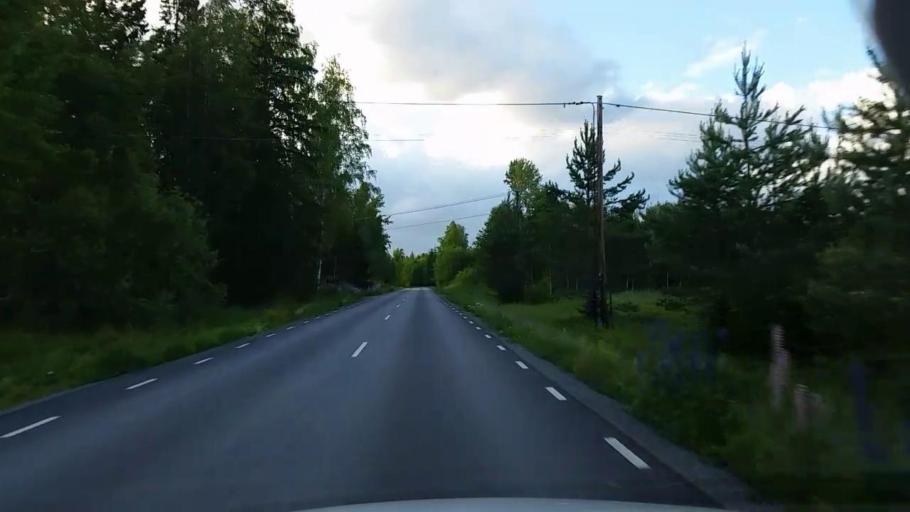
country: SE
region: Vaestmanland
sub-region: Kopings Kommun
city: Kolsva
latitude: 59.6752
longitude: 15.8405
